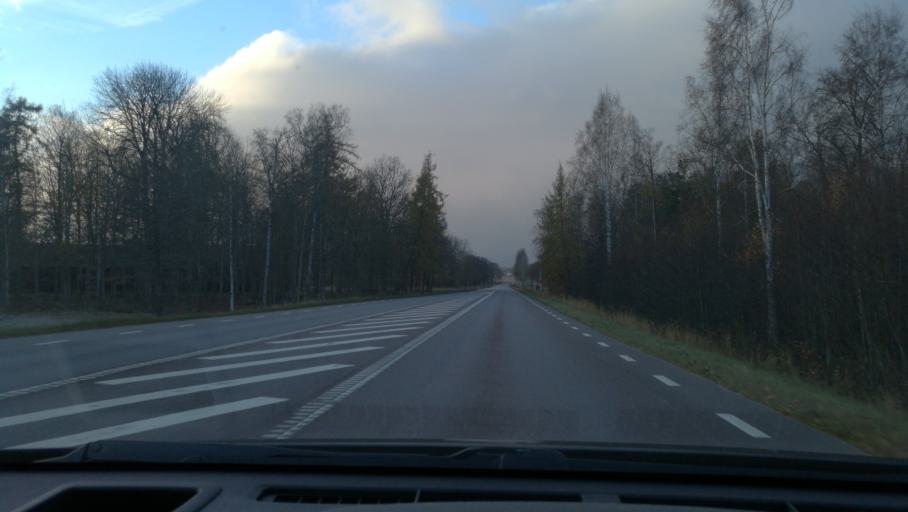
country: SE
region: Soedermanland
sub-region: Vingakers Kommun
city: Vingaker
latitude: 59.1502
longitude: 16.0484
